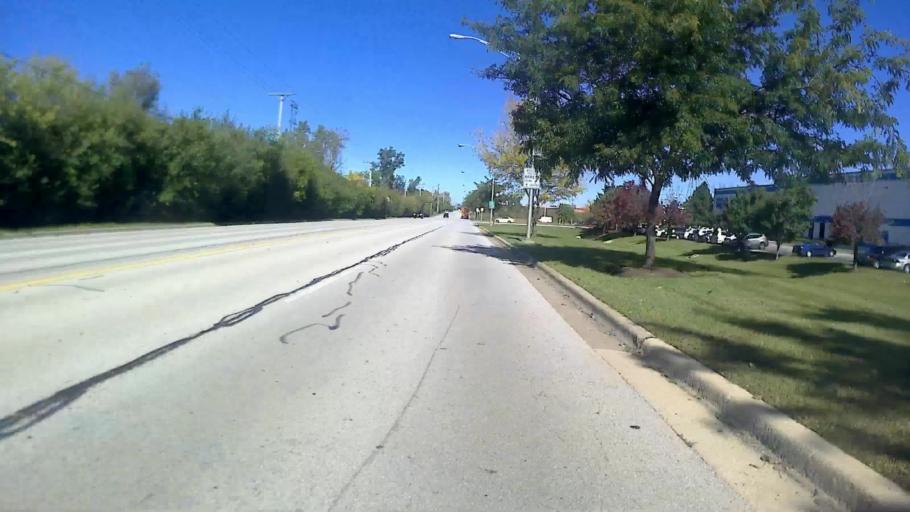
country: US
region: Illinois
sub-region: DuPage County
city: Villa Park
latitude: 41.9102
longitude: -88.0079
